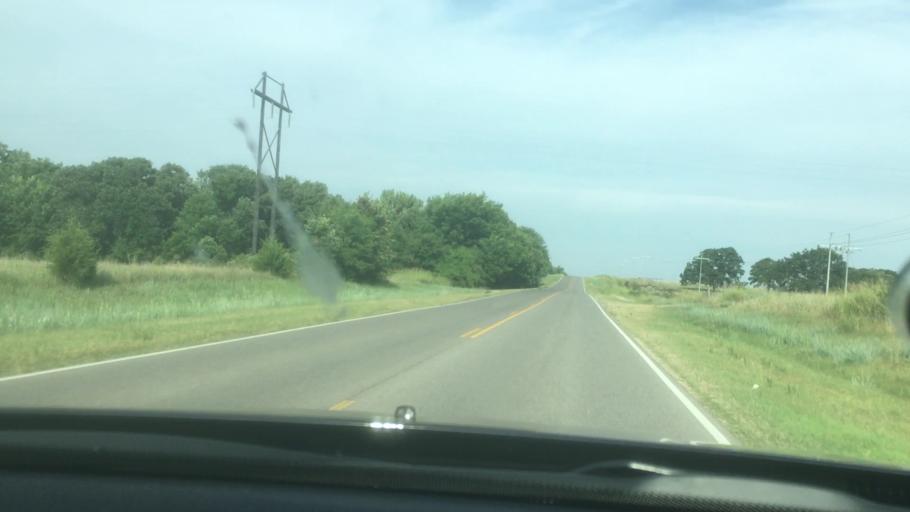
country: US
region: Oklahoma
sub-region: Garvin County
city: Stratford
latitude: 34.7968
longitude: -96.8260
